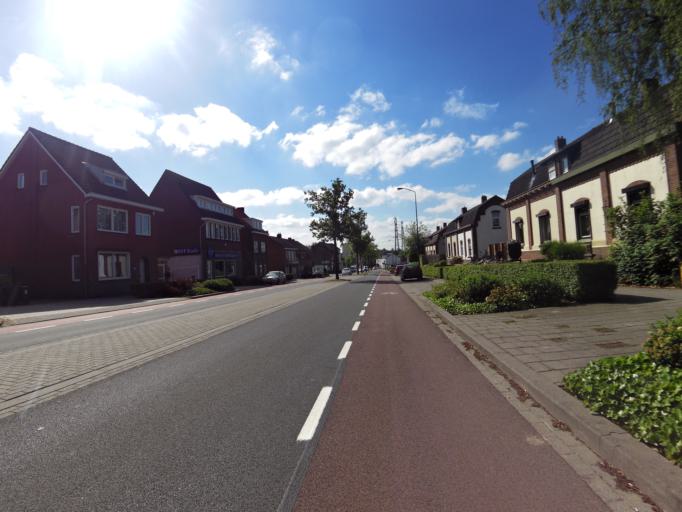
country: NL
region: Limburg
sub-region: Gemeente Heerlen
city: Heerlen
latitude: 50.9052
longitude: 5.9676
